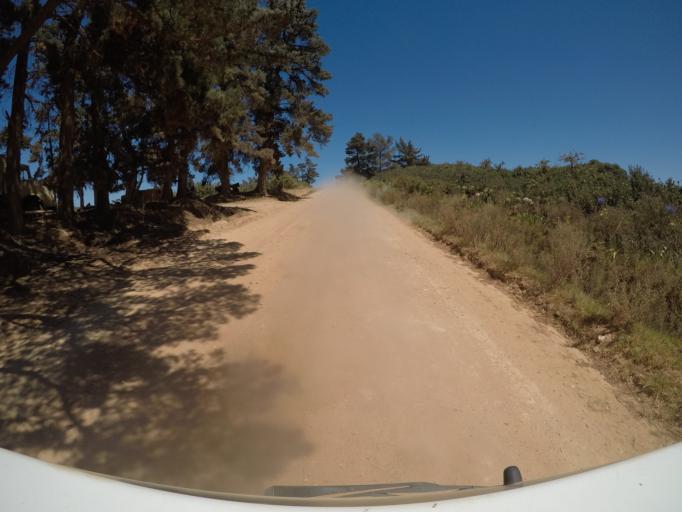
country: ZA
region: Western Cape
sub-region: Overberg District Municipality
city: Grabouw
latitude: -34.2427
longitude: 19.0935
